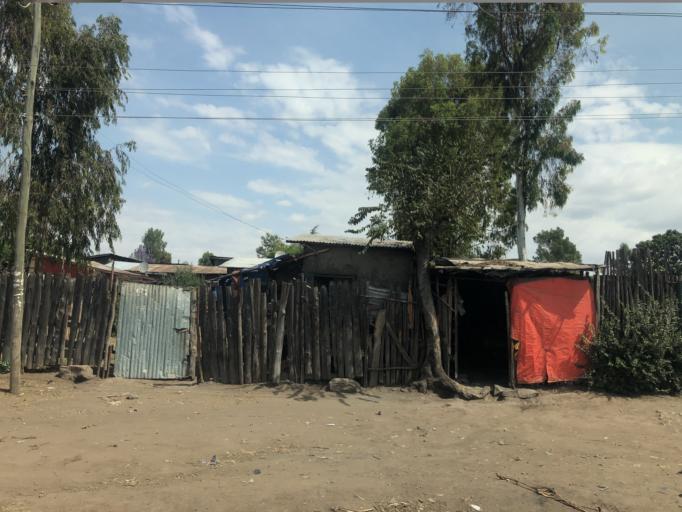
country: ET
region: Oromiya
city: Shashemene
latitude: 7.3425
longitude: 38.6701
